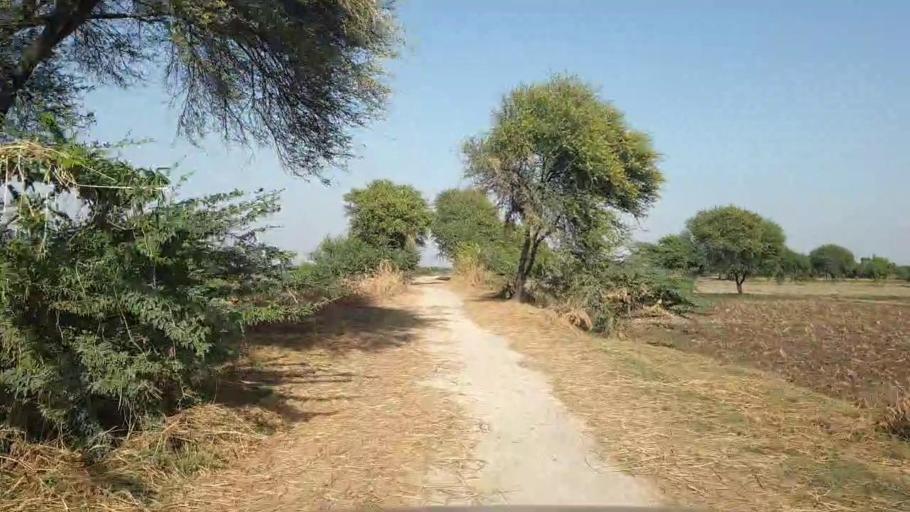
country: PK
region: Sindh
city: Rajo Khanani
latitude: 25.0039
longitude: 68.7558
